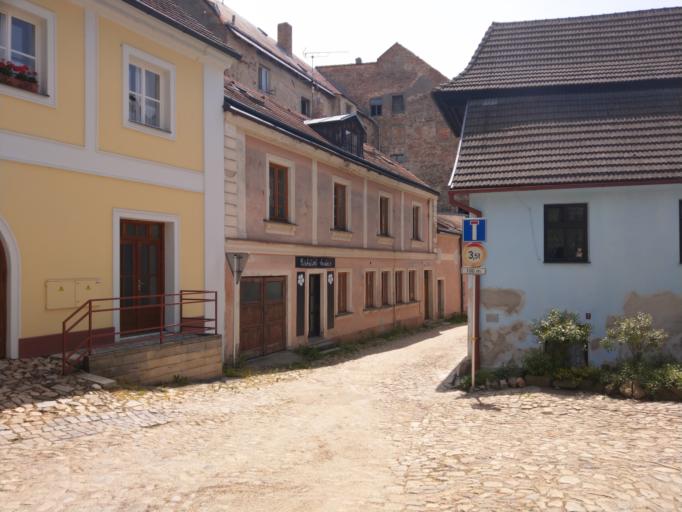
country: CZ
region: Jihocesky
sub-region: Okres Jindrichuv Hradec
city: Jindrichuv Hradec
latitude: 49.1435
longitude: 14.9998
